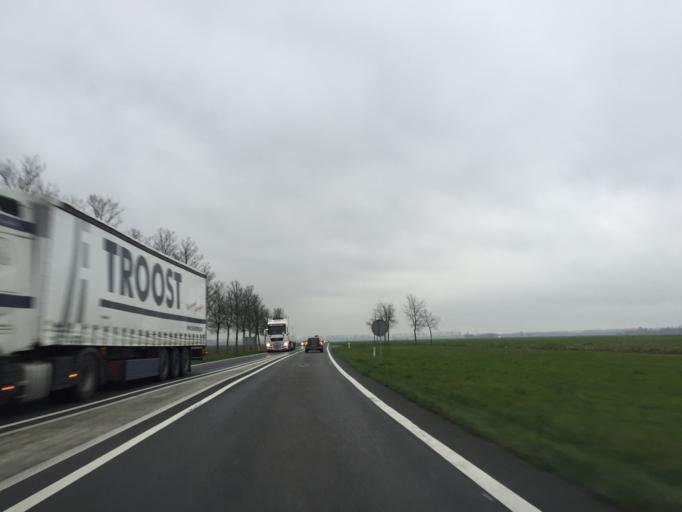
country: NL
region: Zeeland
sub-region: Gemeente Terneuzen
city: Westdorpe
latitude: 51.2440
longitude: 3.8586
